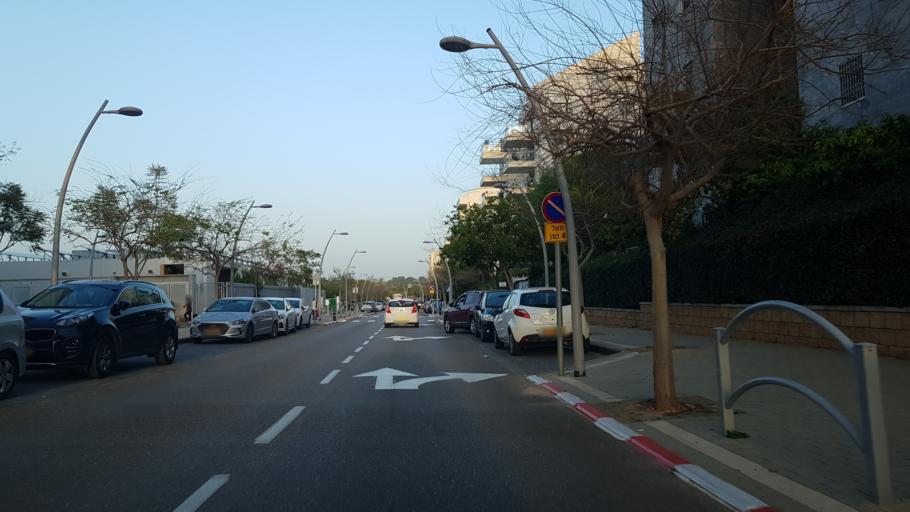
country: IL
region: Central District
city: Ra'anana
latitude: 32.1978
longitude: 34.8907
